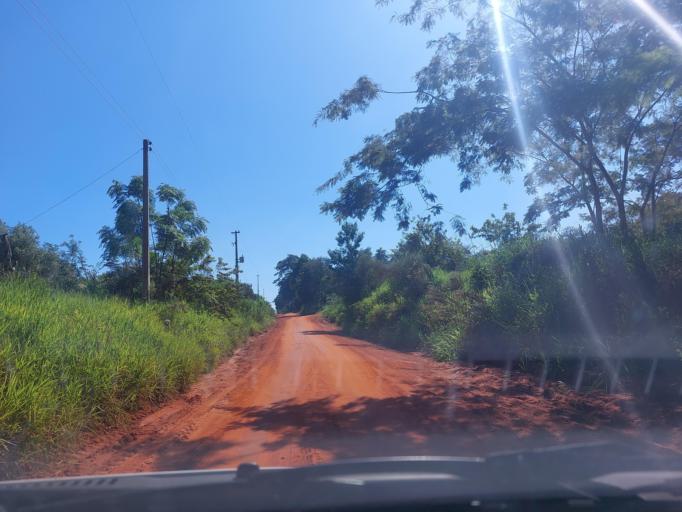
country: PY
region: San Pedro
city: Lima
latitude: -24.1679
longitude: -56.0134
